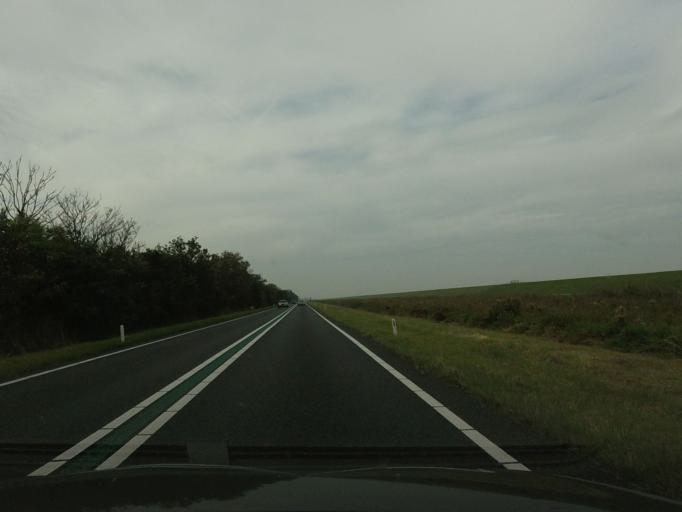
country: NL
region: North Holland
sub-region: Gemeente Den Helder
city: Den Helder
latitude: 52.8922
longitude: 4.8564
